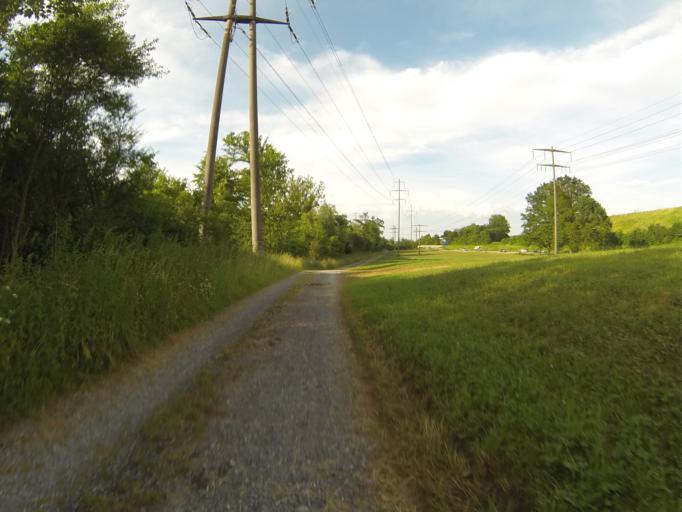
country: CH
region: Lucerne
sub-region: Lucerne-Land District
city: Buchrain
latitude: 47.0954
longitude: 8.3362
